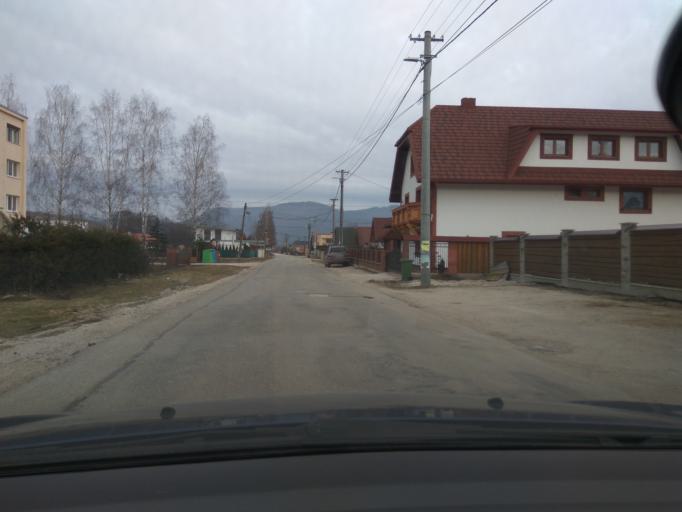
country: SK
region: Zilinsky
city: Rajec
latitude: 49.1025
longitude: 18.6837
